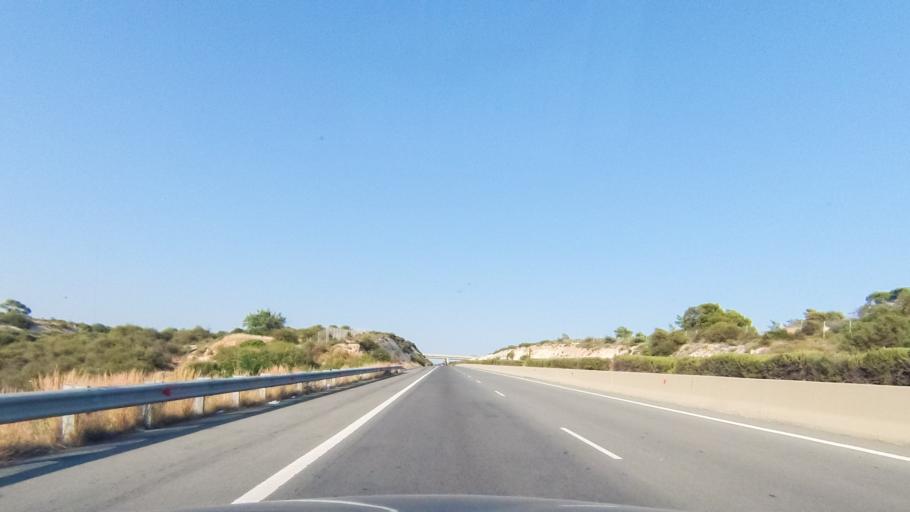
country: CY
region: Limassol
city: Sotira
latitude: 34.6897
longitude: 32.8133
